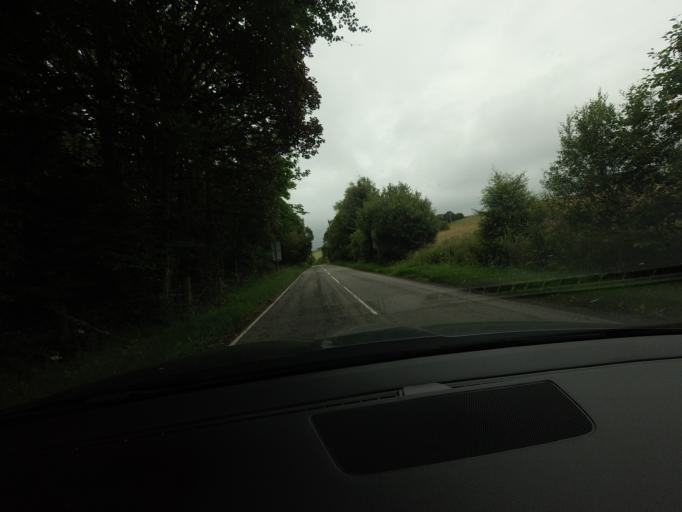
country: GB
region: Scotland
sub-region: Highland
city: Alness
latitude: 58.0293
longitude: -4.4100
